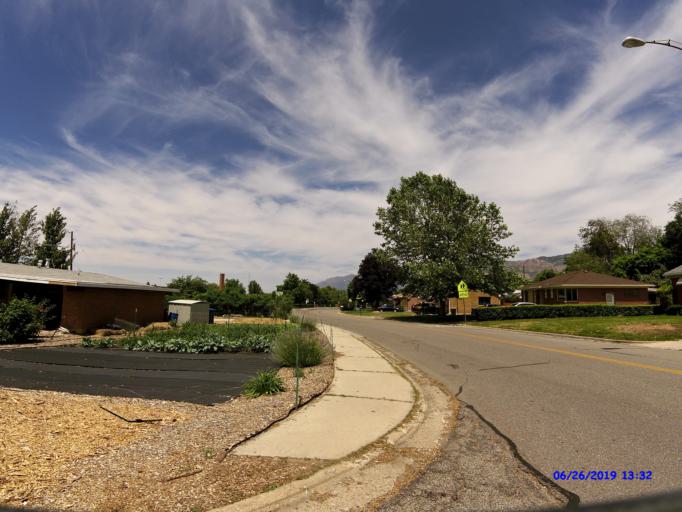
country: US
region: Utah
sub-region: Weber County
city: South Ogden
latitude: 41.2028
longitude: -111.9582
